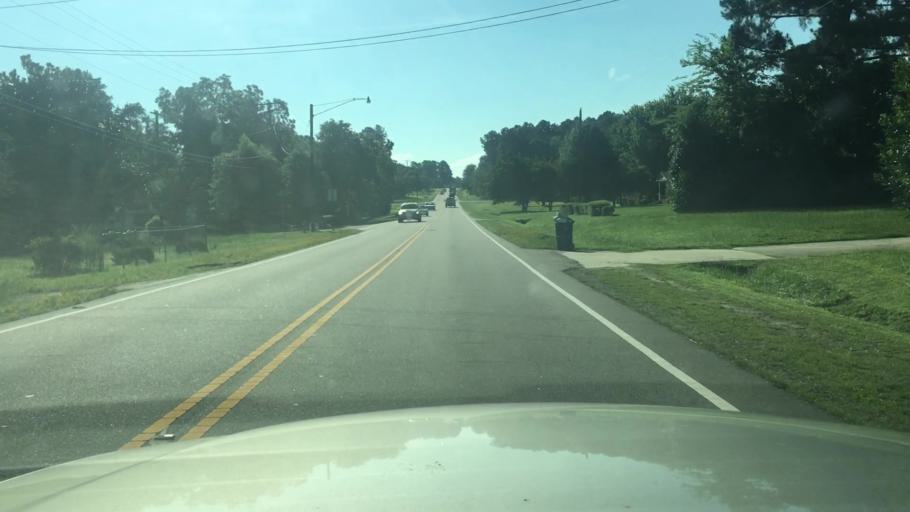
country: US
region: North Carolina
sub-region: Cumberland County
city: Fayetteville
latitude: 35.1333
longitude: -78.8899
